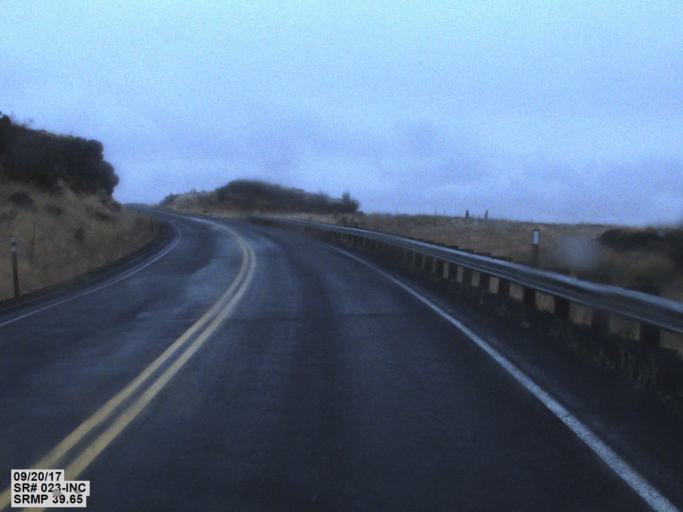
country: US
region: Washington
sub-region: Spokane County
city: Medical Lake
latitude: 47.2639
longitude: -117.9291
